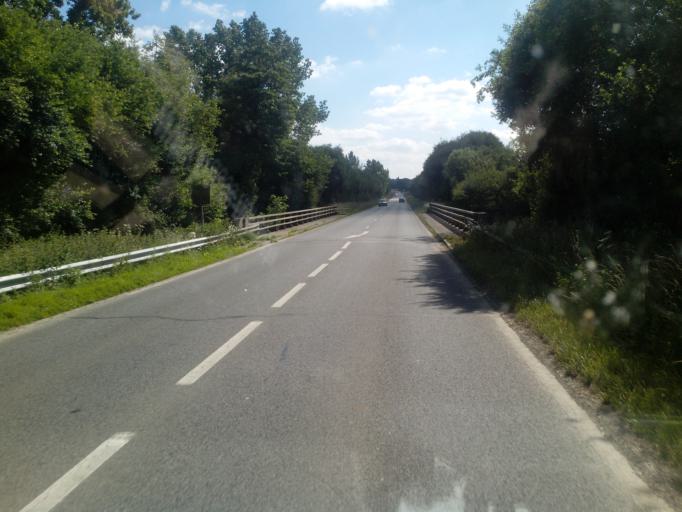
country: FR
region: Brittany
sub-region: Departement d'Ille-et-Vilaine
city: Acigne
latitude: 48.1304
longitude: -1.5223
